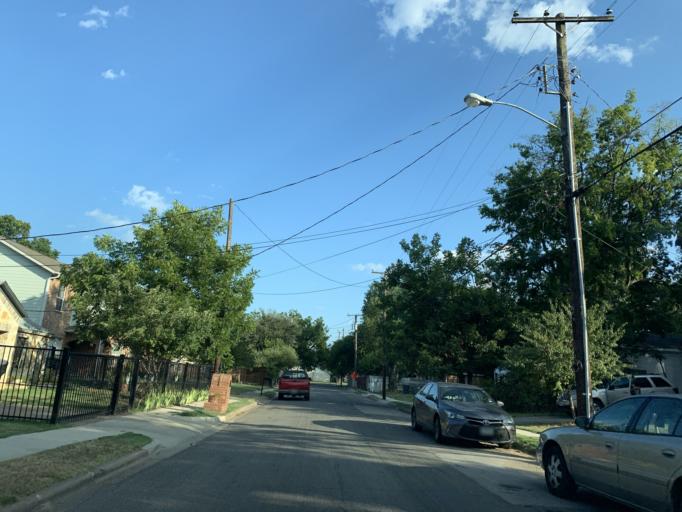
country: US
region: Texas
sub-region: Dallas County
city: Hutchins
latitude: 32.7014
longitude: -96.7807
